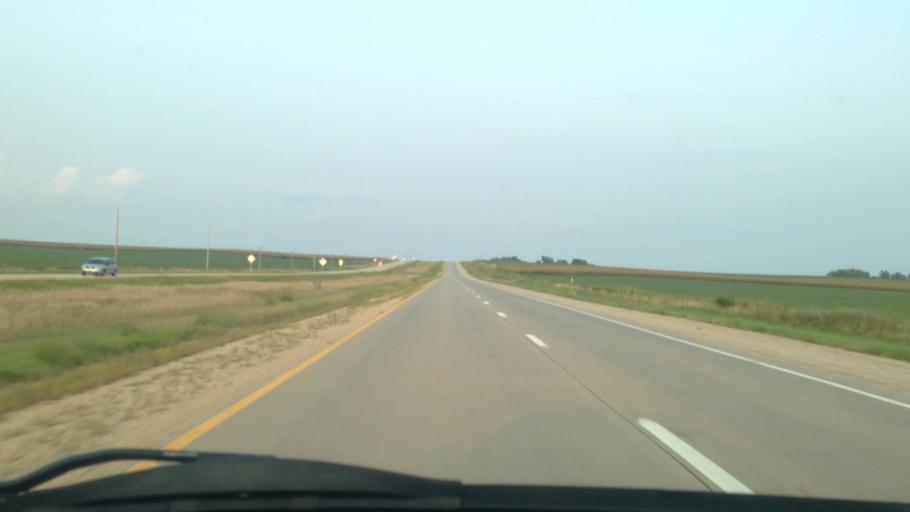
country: US
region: Iowa
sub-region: Benton County
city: Atkins
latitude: 41.9633
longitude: -91.9840
